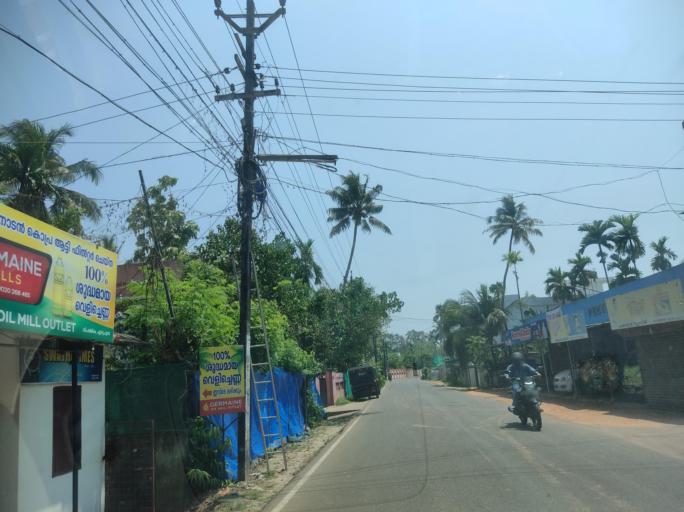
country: IN
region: Kerala
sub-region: Alappuzha
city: Kutiatodu
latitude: 9.8260
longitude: 76.2983
